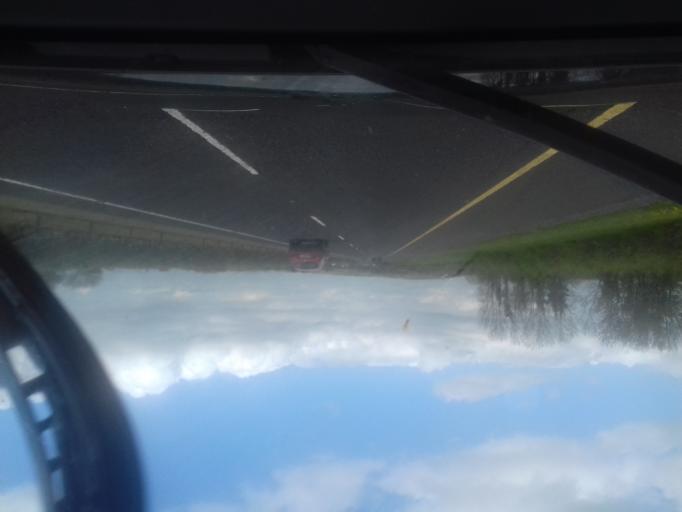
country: IE
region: Leinster
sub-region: Kildare
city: Monasterevin
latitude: 53.1093
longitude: -7.1219
